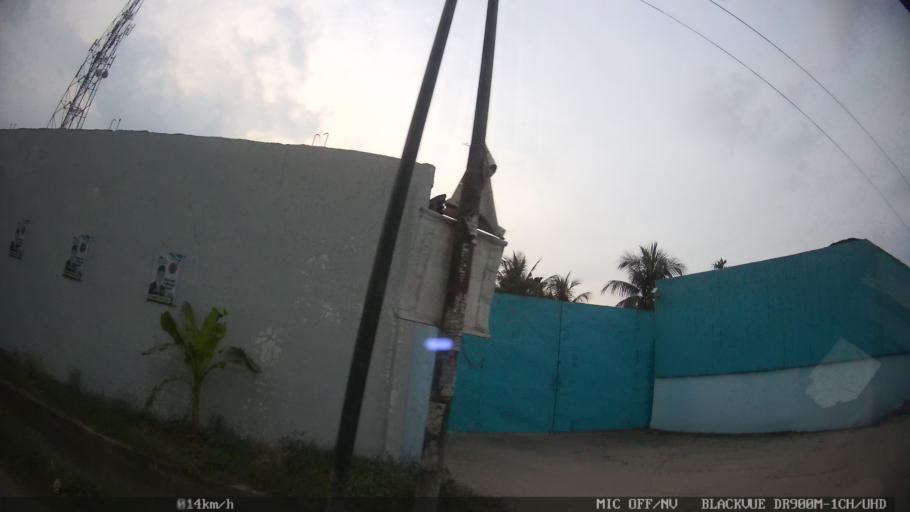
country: ID
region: North Sumatra
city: Sunggal
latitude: 3.5843
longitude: 98.5923
